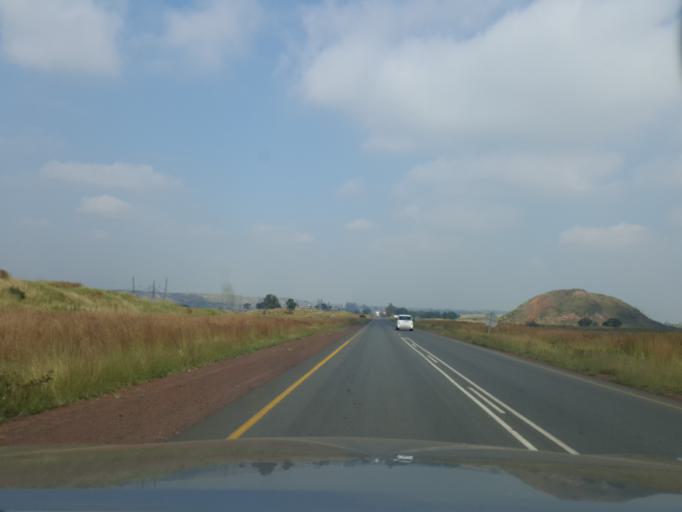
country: ZA
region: Mpumalanga
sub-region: Nkangala District Municipality
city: Witbank
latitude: -26.0144
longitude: 29.3861
